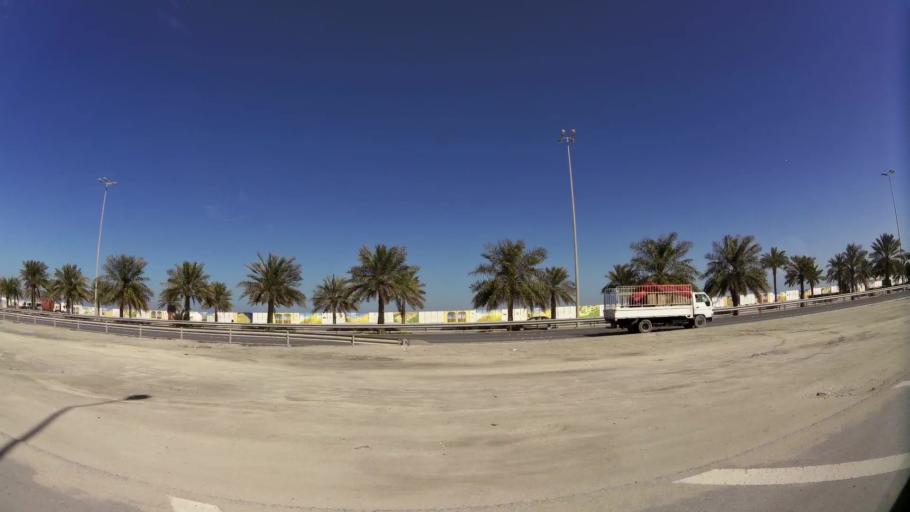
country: BH
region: Muharraq
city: Al Hadd
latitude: 26.2395
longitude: 50.6576
